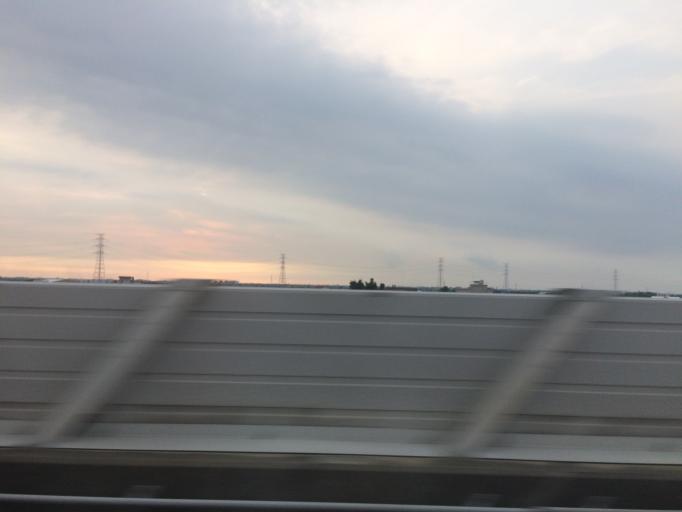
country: TW
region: Taiwan
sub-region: Chiayi
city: Taibao
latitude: 23.6408
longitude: 120.3511
